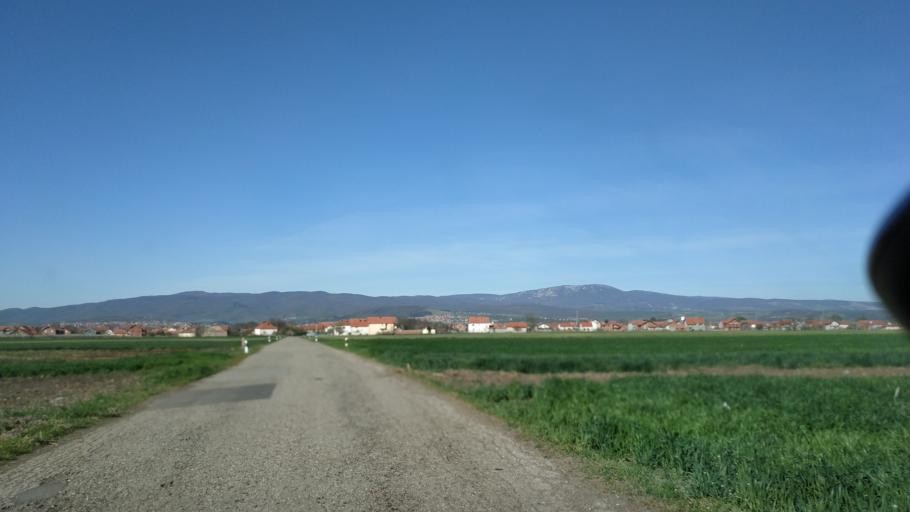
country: RS
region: Central Serbia
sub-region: Nisavski Okrug
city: Aleksinac
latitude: 43.5043
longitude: 21.6811
